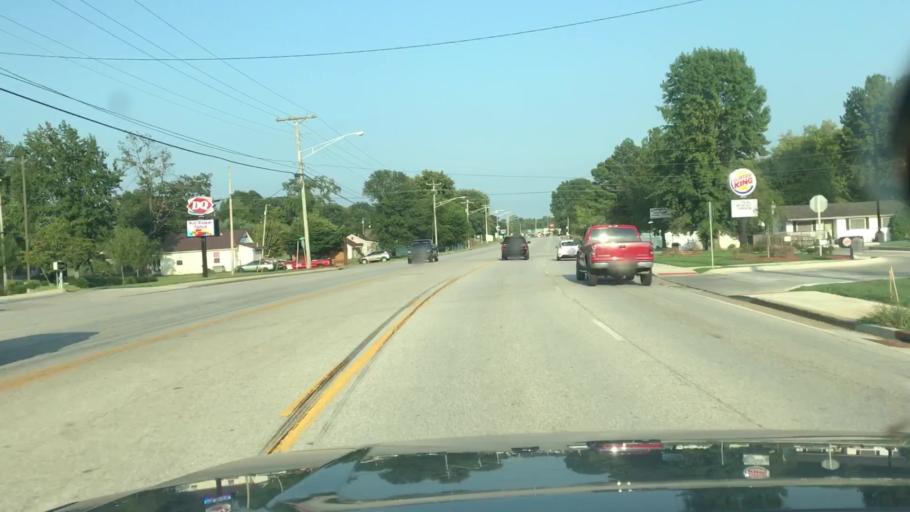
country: US
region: Tennessee
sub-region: Sumner County
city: Portland
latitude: 36.5774
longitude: -86.5229
